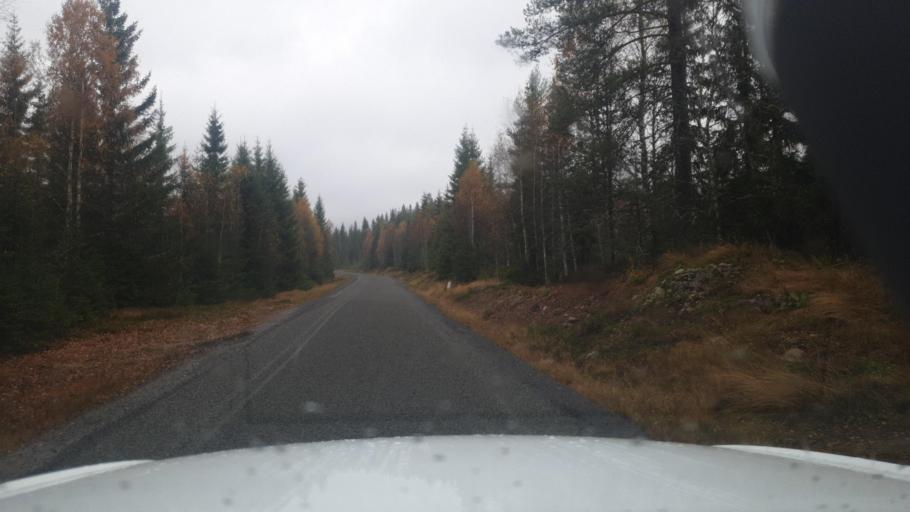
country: SE
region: Vaermland
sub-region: Eda Kommun
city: Charlottenberg
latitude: 60.1236
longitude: 12.5986
